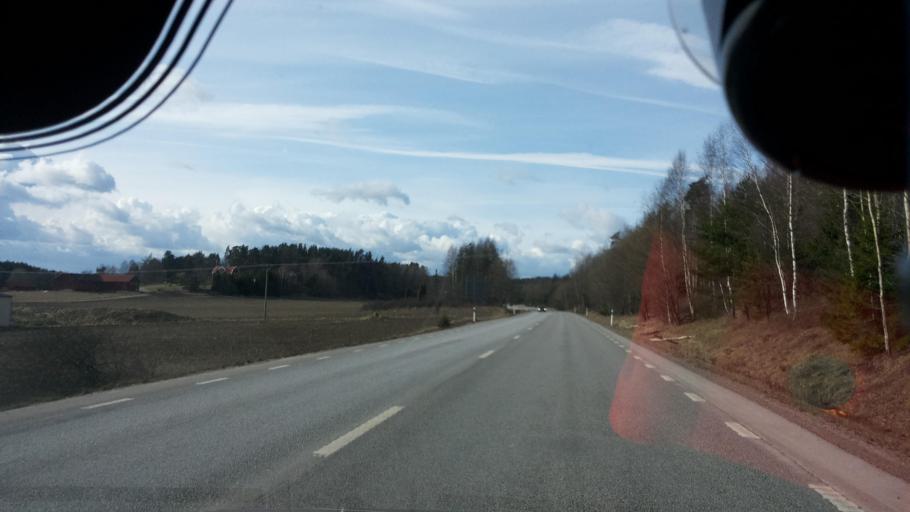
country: SE
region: Soedermanland
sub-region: Trosa Kommun
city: Vagnharad
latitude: 58.9560
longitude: 17.4948
